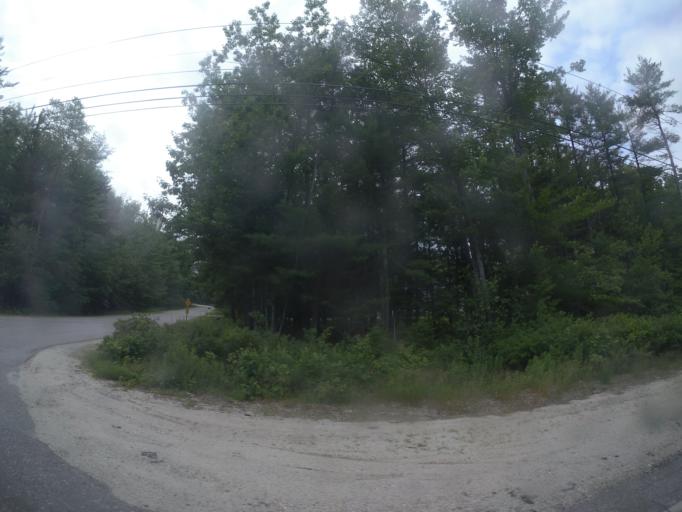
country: US
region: Maine
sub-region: Cumberland County
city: Falmouth
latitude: 43.7570
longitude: -70.2423
